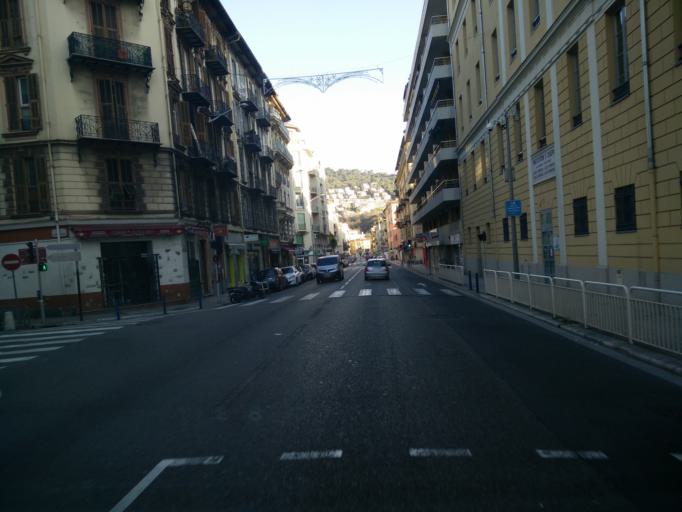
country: FR
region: Provence-Alpes-Cote d'Azur
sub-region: Departement des Alpes-Maritimes
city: Nice
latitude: 43.7019
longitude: 7.2826
